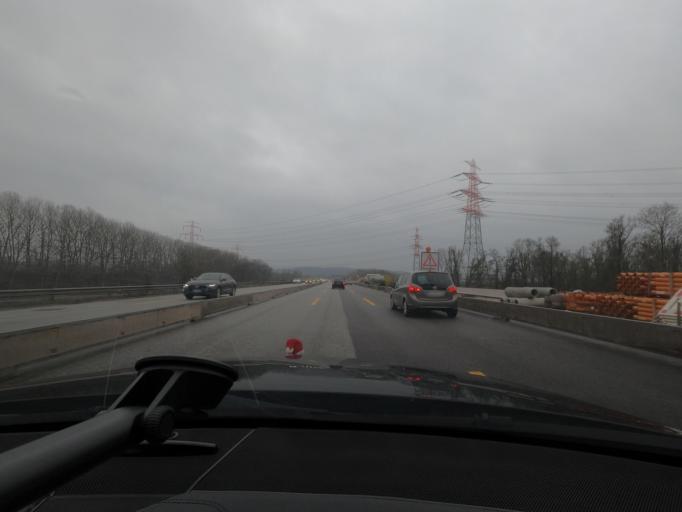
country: DE
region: Hamburg
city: Altona
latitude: 53.4880
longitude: 9.9140
